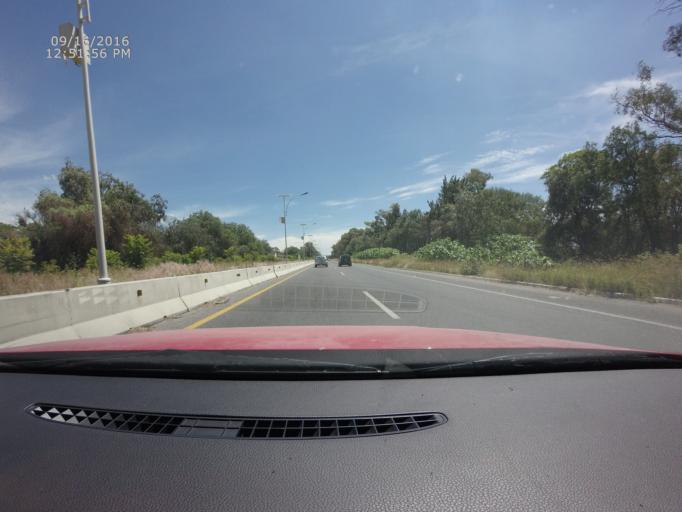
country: MX
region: Queretaro
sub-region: Colon
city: Purisima de Cubos (La Purisima)
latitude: 20.6166
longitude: -100.1505
